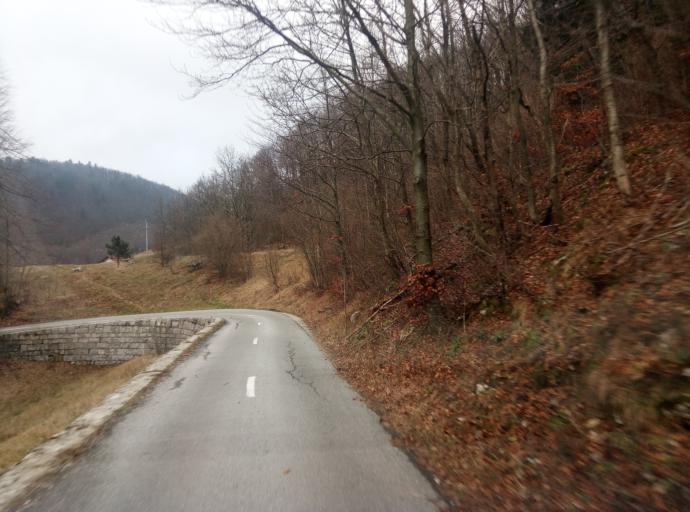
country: SI
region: Vipava
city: Vipava
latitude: 45.9076
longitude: 14.0260
